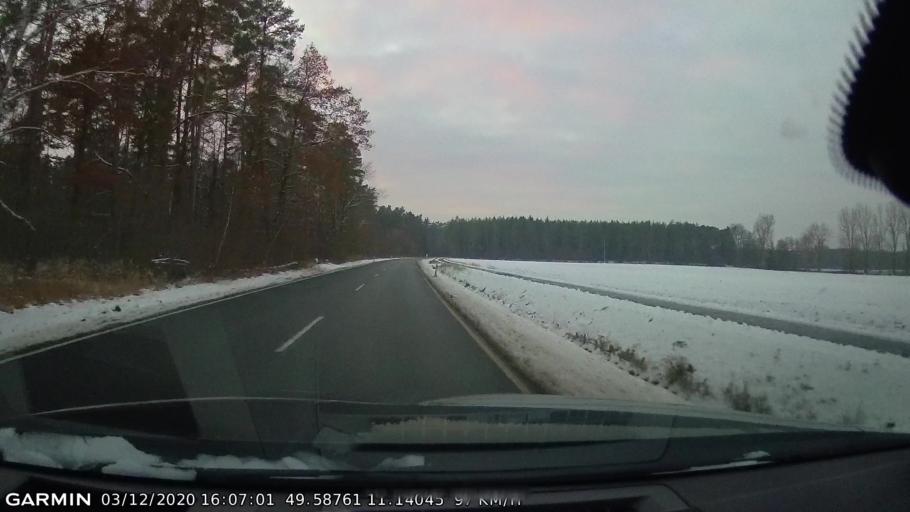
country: DE
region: Bavaria
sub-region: Upper Franconia
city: Kleinsendelbach
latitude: 49.5876
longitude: 11.1400
